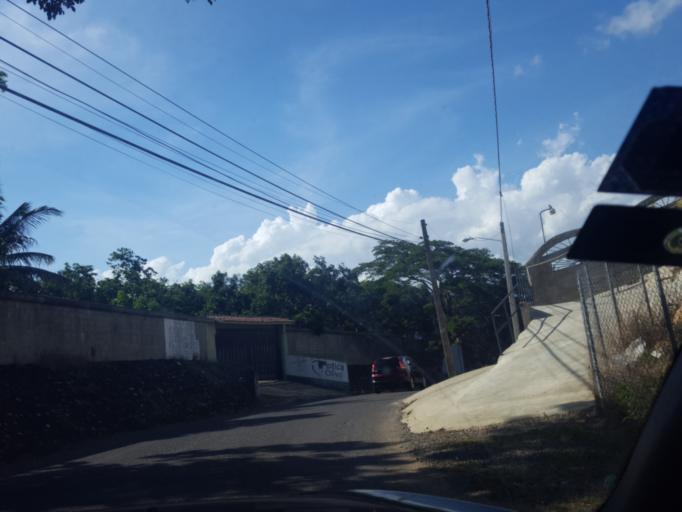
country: DO
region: La Vega
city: Rio Verde Arriba
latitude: 19.3532
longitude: -70.6036
